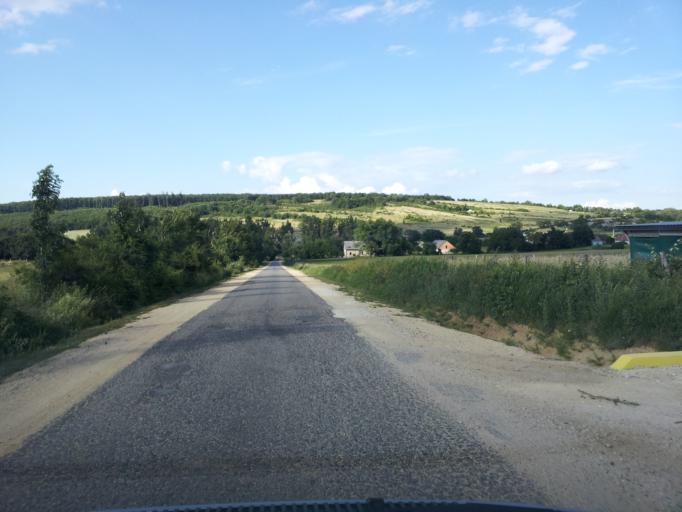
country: HU
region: Veszprem
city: Zirc
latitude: 47.2030
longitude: 17.8453
